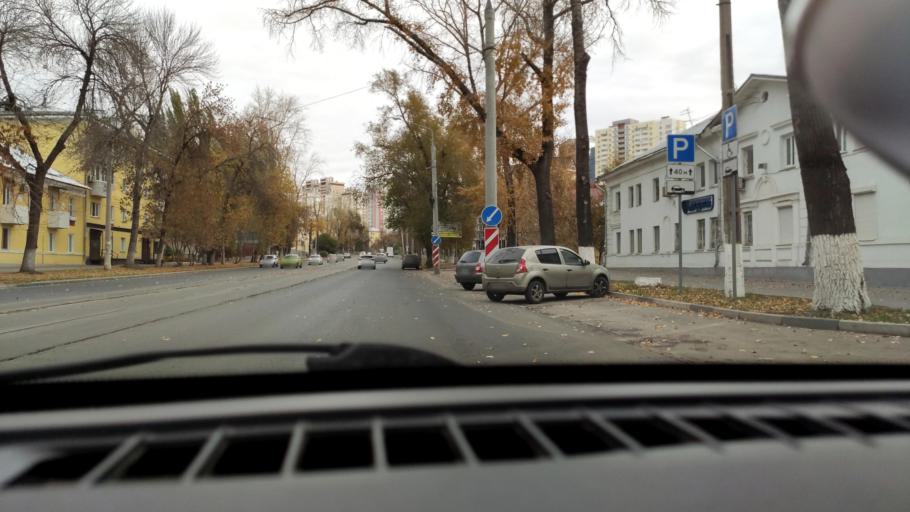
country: RU
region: Samara
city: Samara
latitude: 53.1878
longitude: 50.1272
